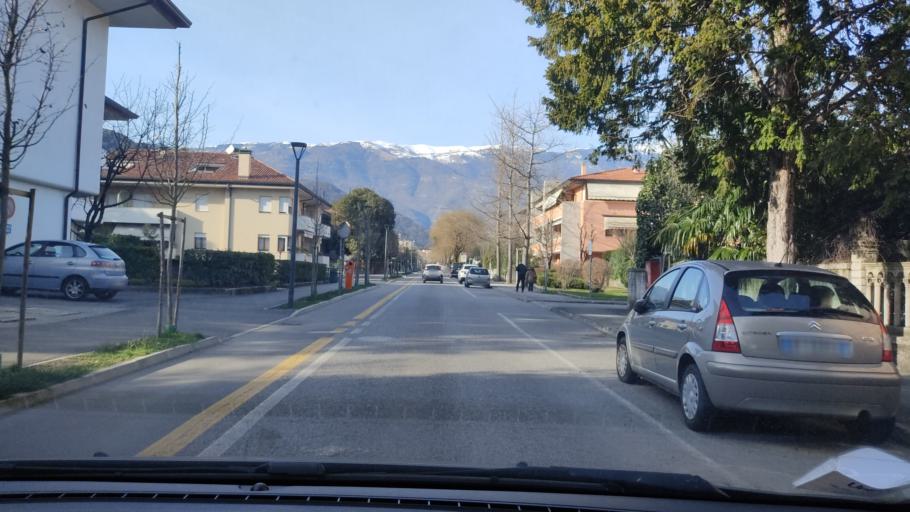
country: IT
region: Veneto
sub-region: Provincia di Treviso
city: Vittorio Veneto
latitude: 45.9809
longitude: 12.3024
